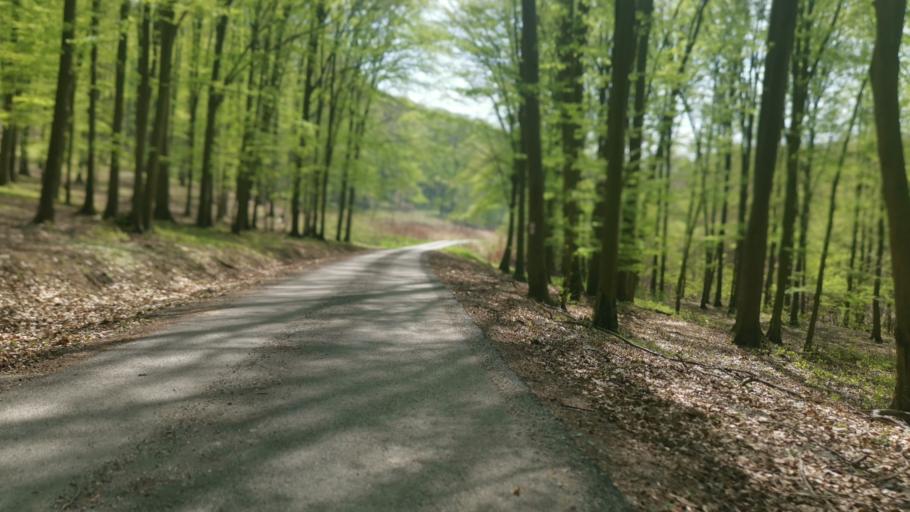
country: SK
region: Nitriansky
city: Brezova pod Bradlom
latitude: 48.5937
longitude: 17.4907
